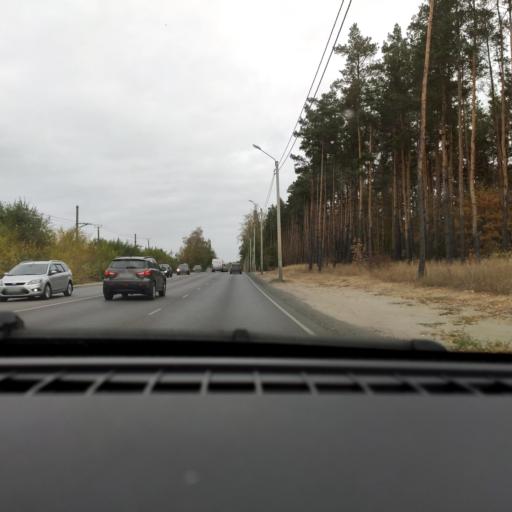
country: RU
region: Voronezj
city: Voronezh
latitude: 51.6754
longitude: 39.2730
